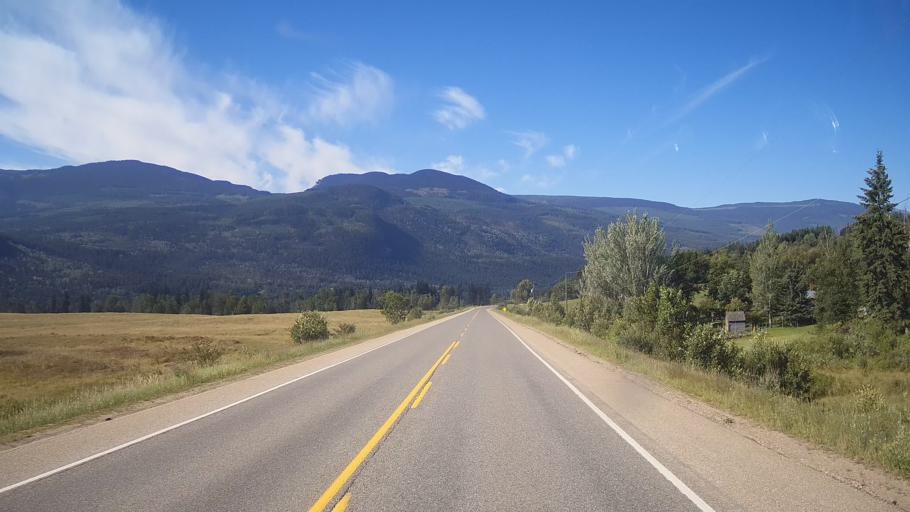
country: CA
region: British Columbia
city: Chase
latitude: 51.6096
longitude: -119.6956
